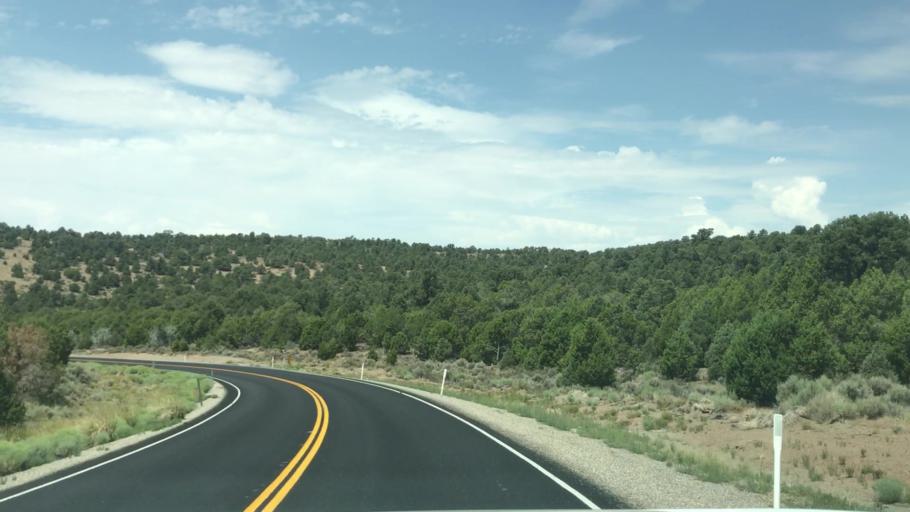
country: US
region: Nevada
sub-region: Eureka County
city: Eureka
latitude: 39.3985
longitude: -115.4724
